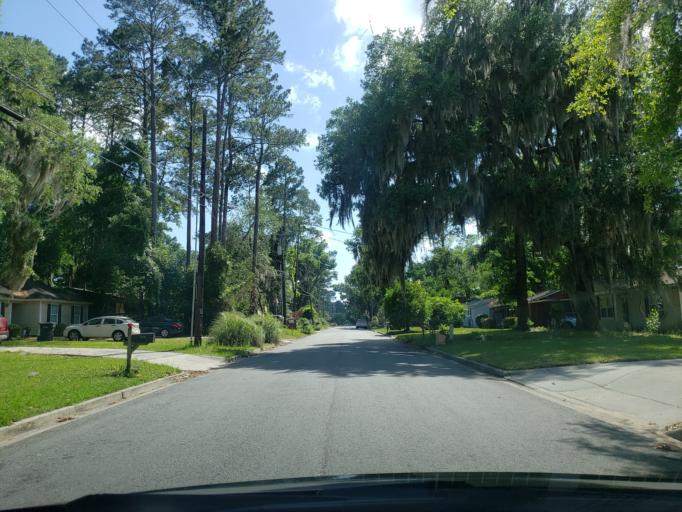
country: US
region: Georgia
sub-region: Chatham County
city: Isle of Hope
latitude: 31.9985
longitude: -81.0648
